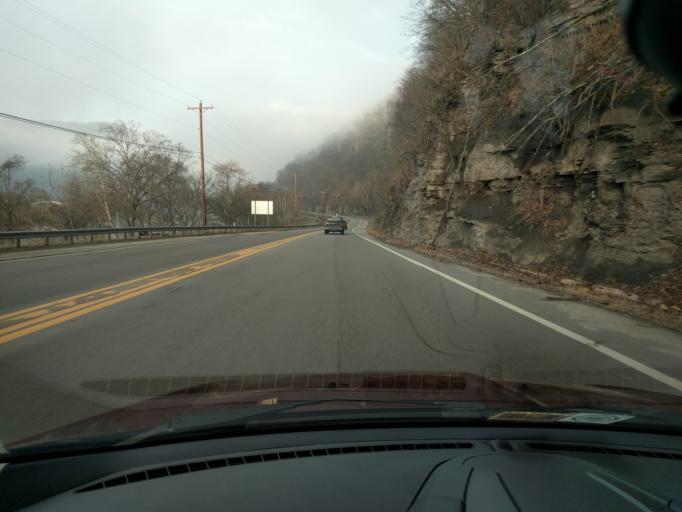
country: US
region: West Virginia
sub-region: Kanawha County
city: Montgomery
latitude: 38.1854
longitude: -81.3206
